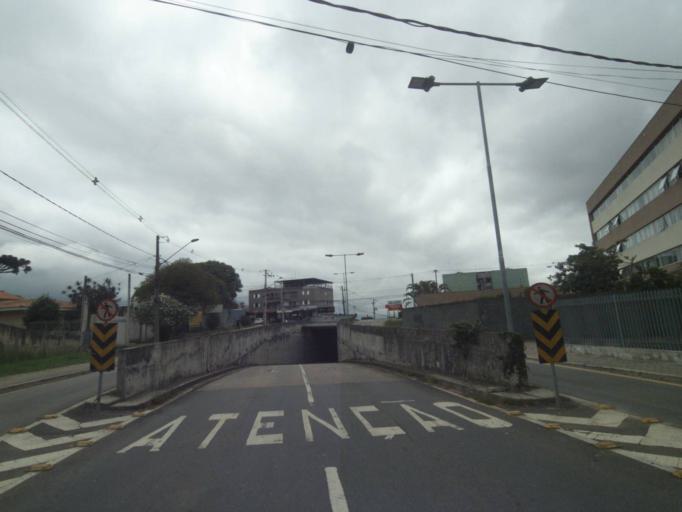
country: BR
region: Parana
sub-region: Curitiba
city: Curitiba
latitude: -25.4383
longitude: -49.2356
